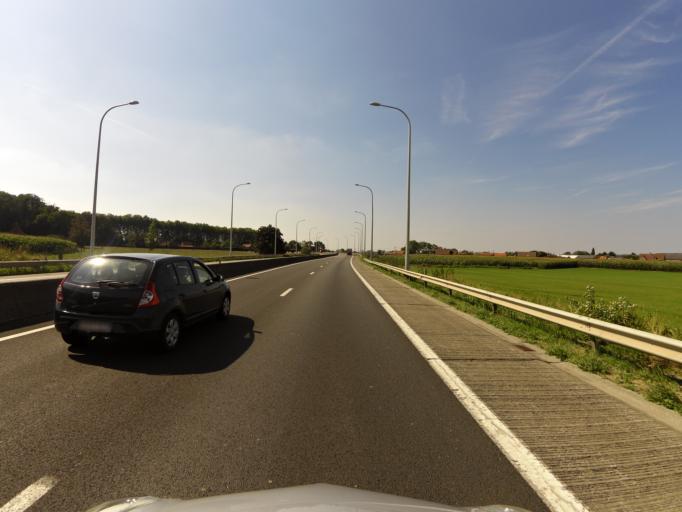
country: BE
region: Flanders
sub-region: Provincie West-Vlaanderen
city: Pittem
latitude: 50.9860
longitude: 3.2529
